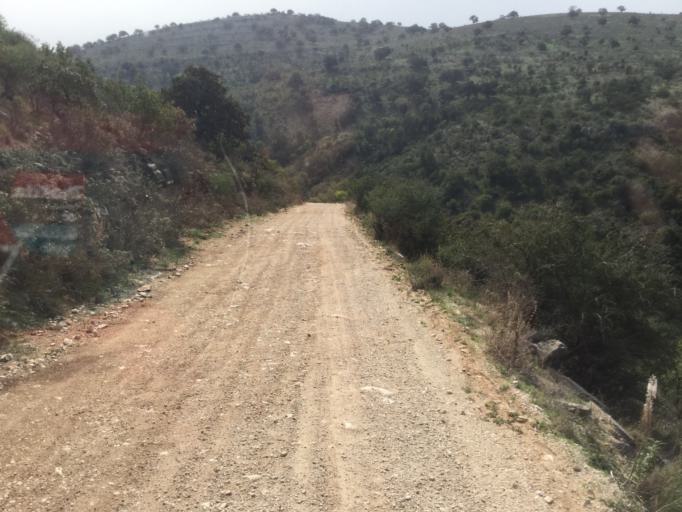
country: GR
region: West Greece
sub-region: Nomos Achaias
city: Lapas
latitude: 38.1755
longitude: 21.3747
